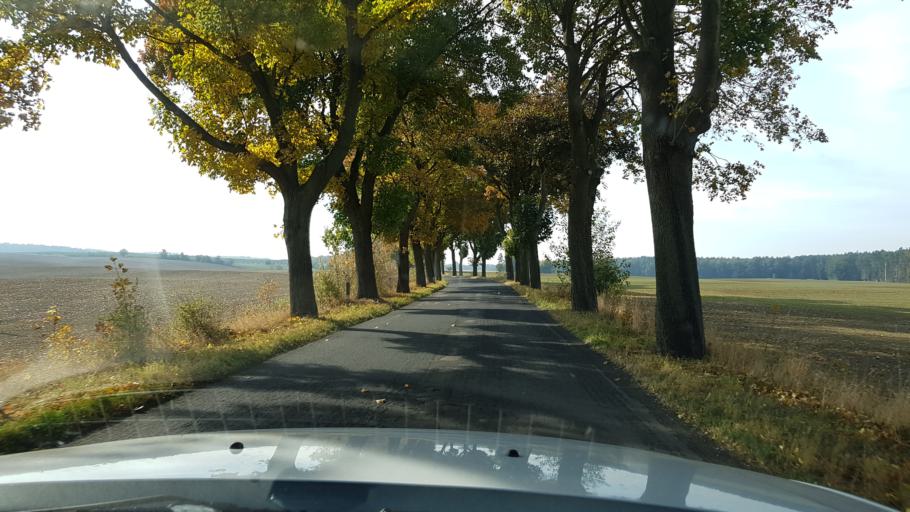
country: PL
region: West Pomeranian Voivodeship
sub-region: Powiat mysliborski
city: Nowogrodek Pomorski
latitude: 52.9528
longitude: 15.1019
